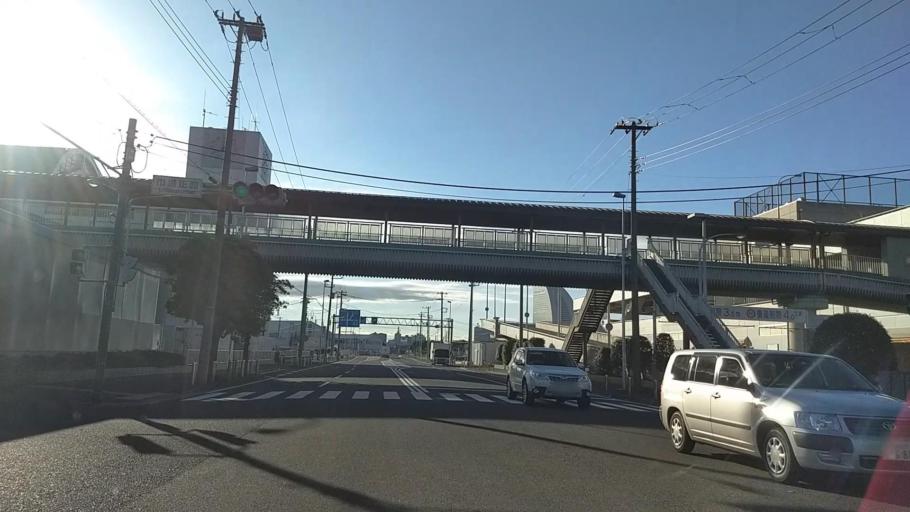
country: JP
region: Kanagawa
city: Yokohama
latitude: 35.4679
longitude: 139.6355
